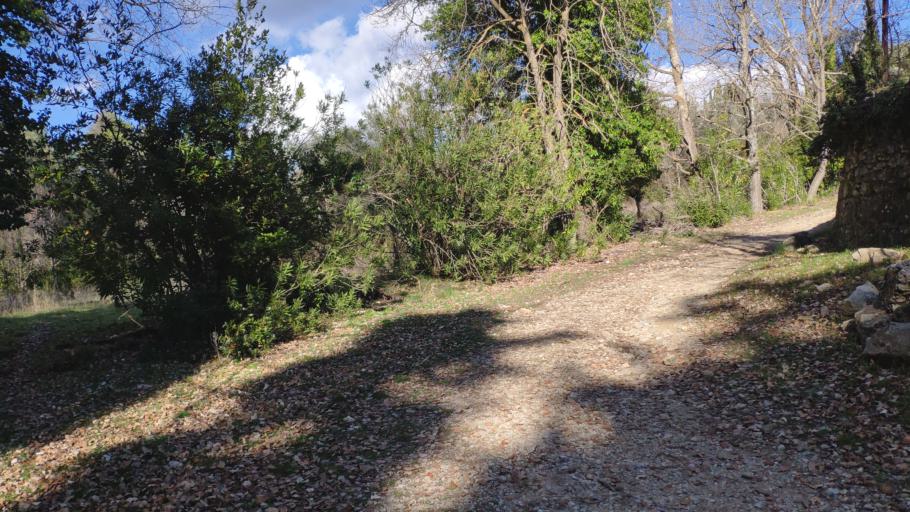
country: GR
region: Attica
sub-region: Nomarchia Anatolikis Attikis
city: Varybobi
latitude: 38.1573
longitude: 23.7948
